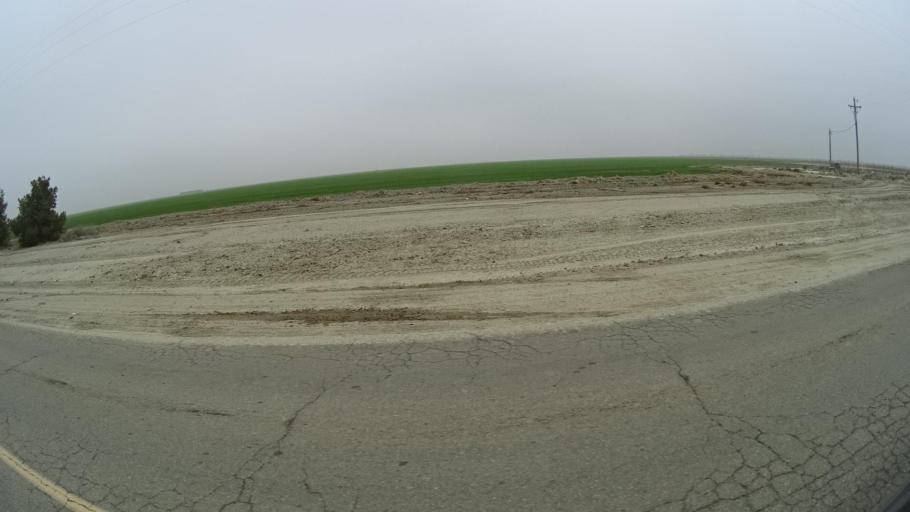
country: US
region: California
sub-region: Kern County
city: Rosedale
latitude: 35.2441
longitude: -119.2528
